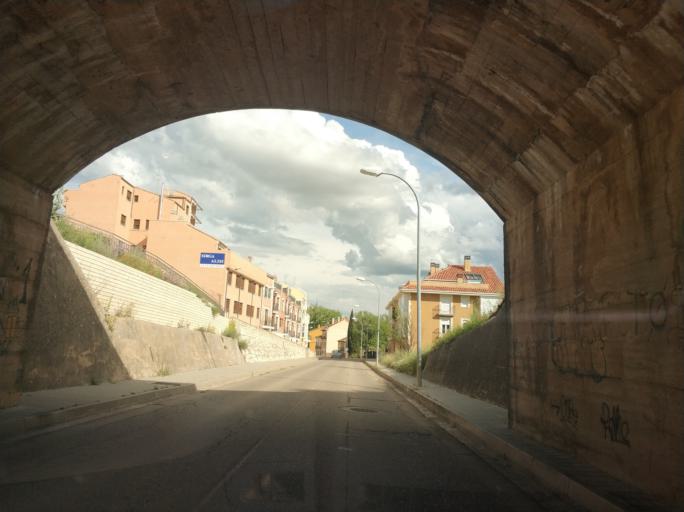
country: ES
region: Castille and Leon
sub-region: Provincia de Burgos
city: Aranda de Duero
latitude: 41.6734
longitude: -3.6938
